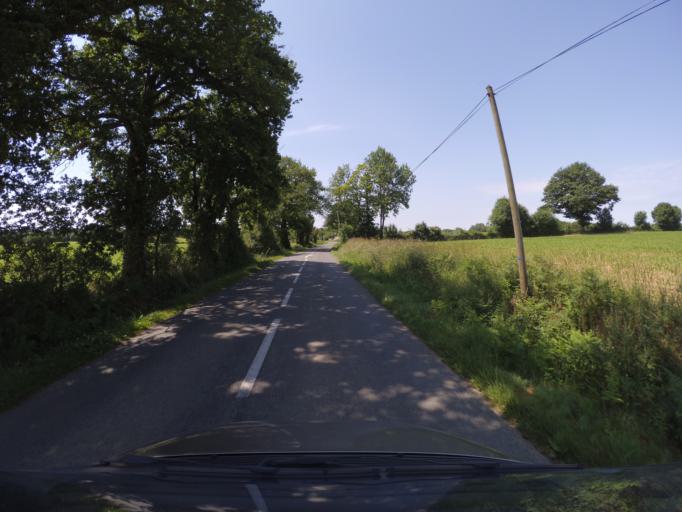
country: FR
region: Pays de la Loire
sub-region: Departement de la Vendee
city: La Flocelliere
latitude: 46.8110
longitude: -0.8570
